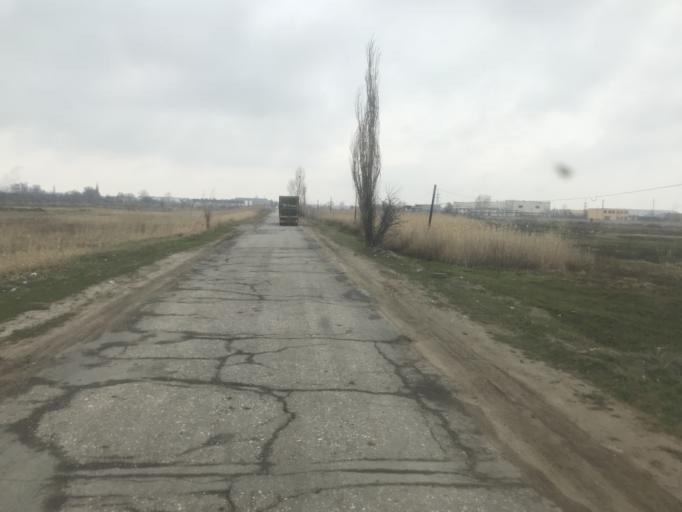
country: RU
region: Volgograd
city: Svetlyy Yar
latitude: 48.5195
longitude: 44.6254
